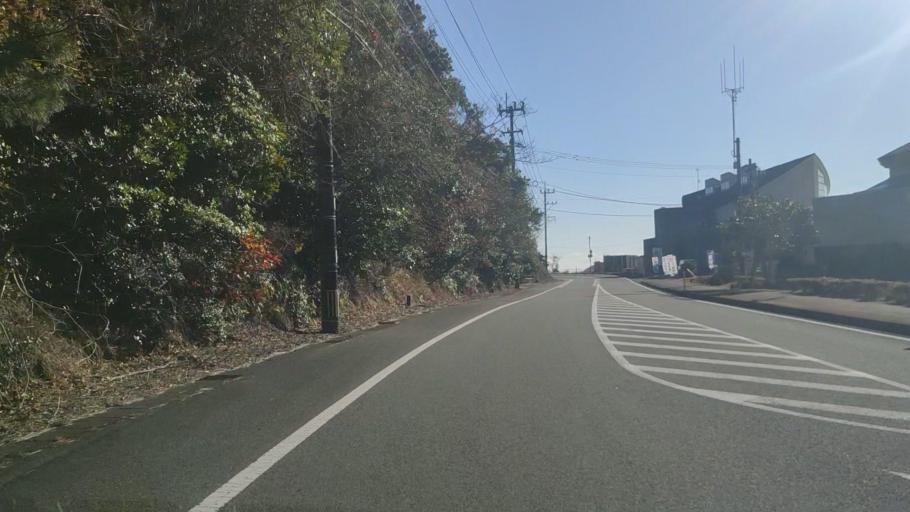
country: JP
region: Miyazaki
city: Nobeoka
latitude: 32.6855
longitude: 131.8006
